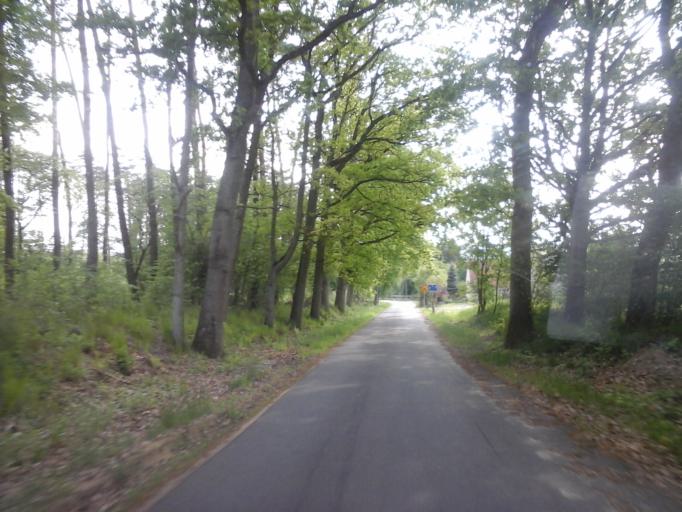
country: PL
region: West Pomeranian Voivodeship
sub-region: Powiat mysliborski
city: Barlinek
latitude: 53.0490
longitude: 15.2179
